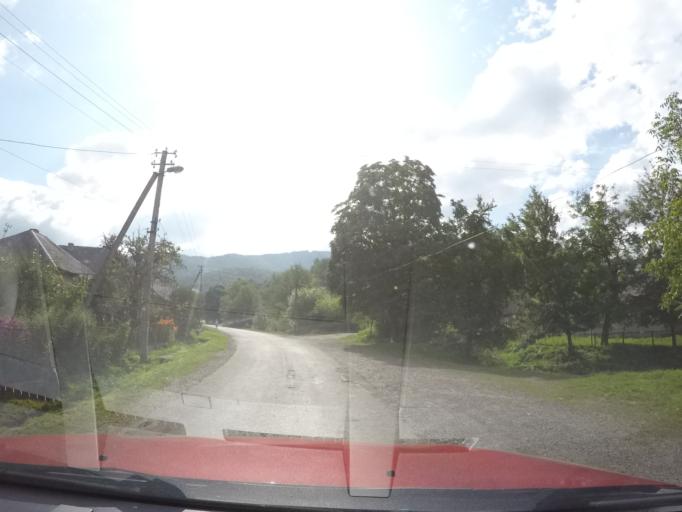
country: UA
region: Zakarpattia
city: Velykyi Bereznyi
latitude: 48.9427
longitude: 22.6236
